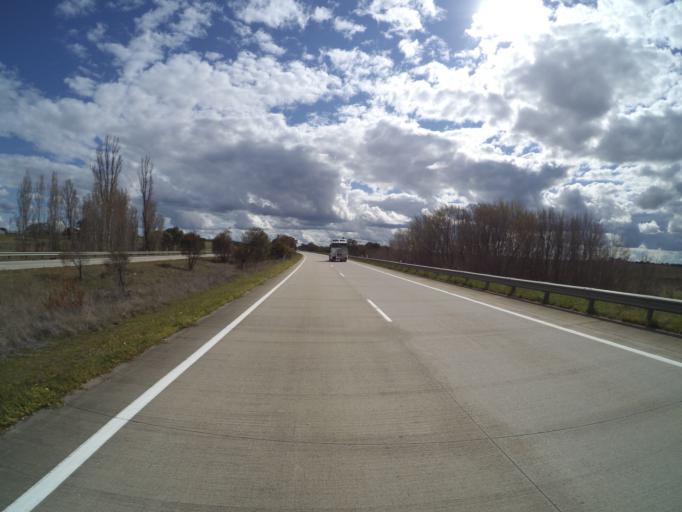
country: AU
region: New South Wales
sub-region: Yass Valley
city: Murrumbateman
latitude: -34.7860
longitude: 149.1866
